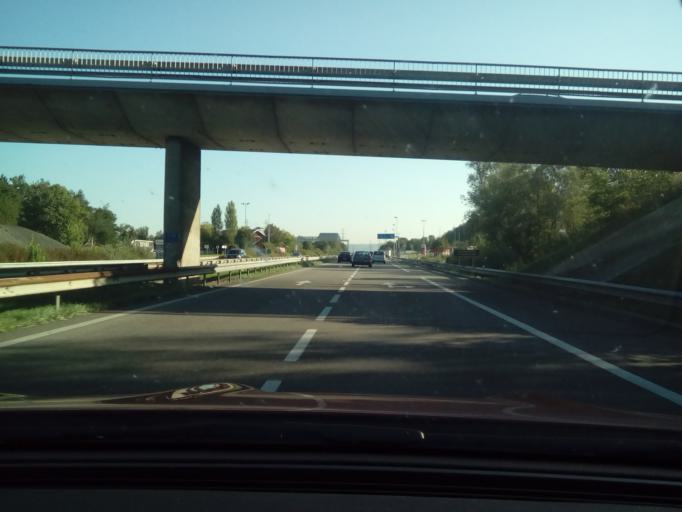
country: FR
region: Rhone-Alpes
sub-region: Departement de la Haute-Savoie
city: Seynod
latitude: 45.8734
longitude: 6.0676
